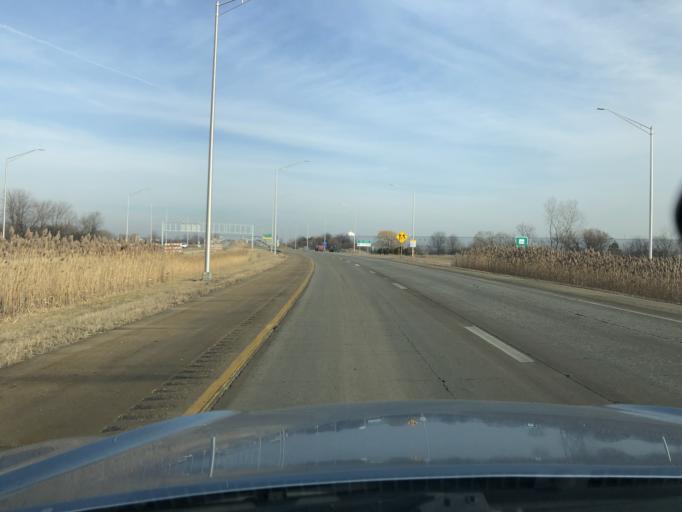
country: US
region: Illinois
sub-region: DuPage County
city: Hanover Park
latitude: 41.9827
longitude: -88.1359
